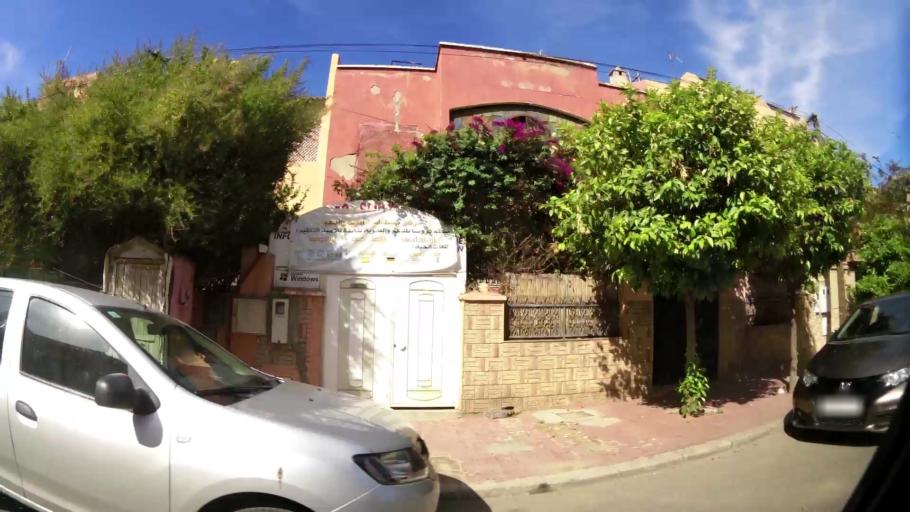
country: MA
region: Marrakech-Tensift-Al Haouz
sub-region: Marrakech
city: Marrakesh
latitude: 31.6534
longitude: -8.0159
